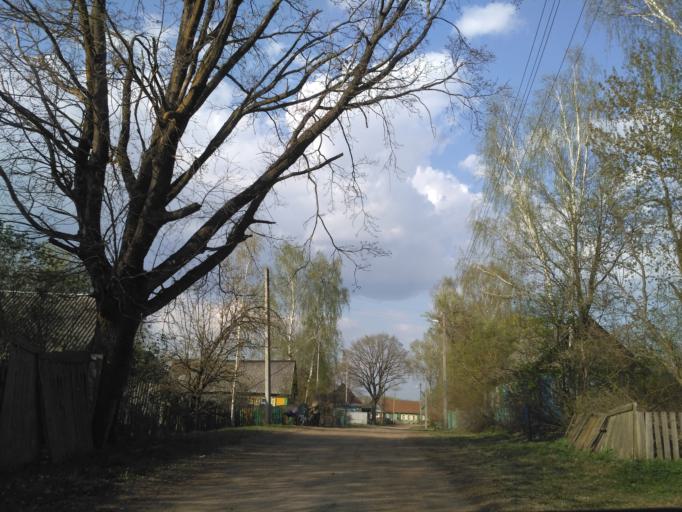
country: BY
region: Minsk
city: Khalopyenichy
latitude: 54.5055
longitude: 28.8505
